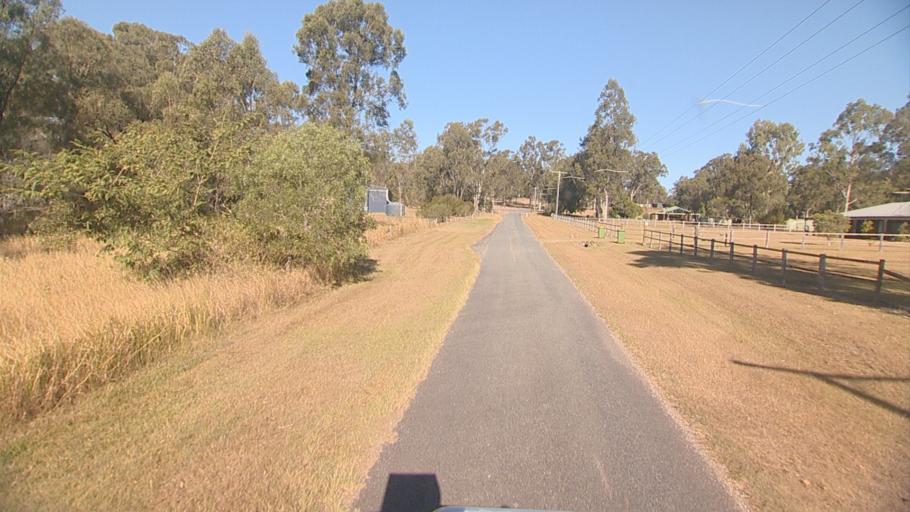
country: AU
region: Queensland
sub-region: Logan
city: Cedar Vale
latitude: -27.8648
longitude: 153.0263
